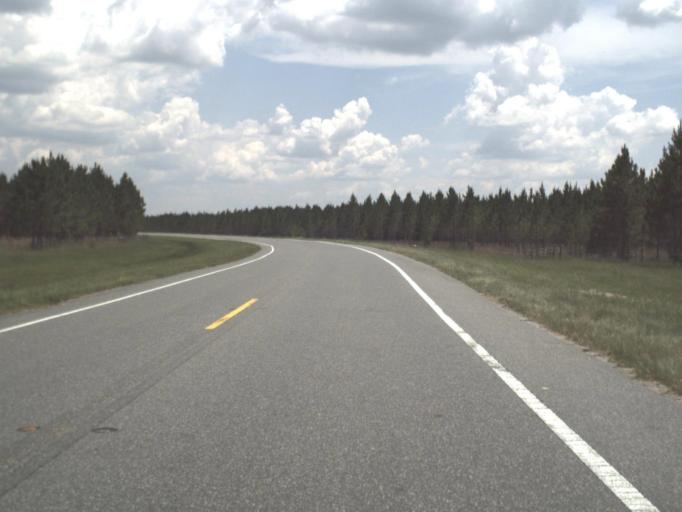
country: US
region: Florida
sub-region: Bradford County
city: Starke
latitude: 30.0058
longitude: -82.0527
